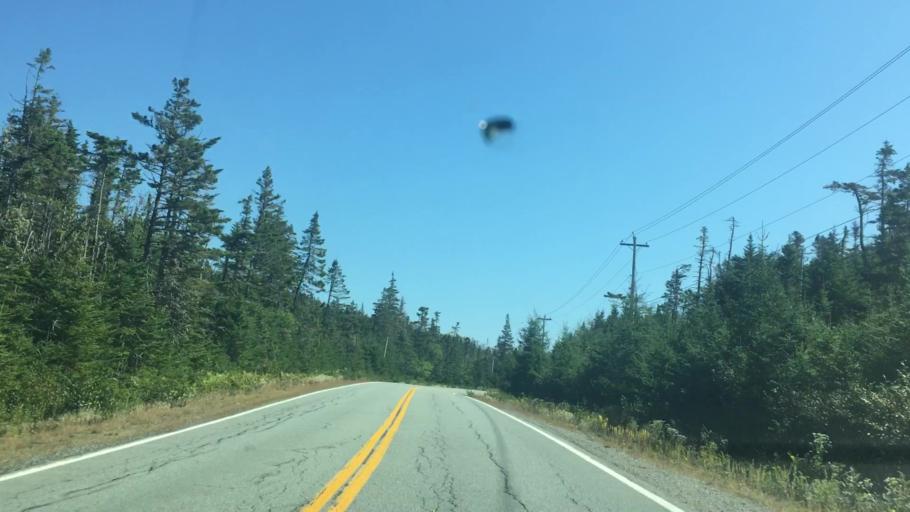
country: CA
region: Nova Scotia
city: Antigonish
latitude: 45.0069
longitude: -62.0862
